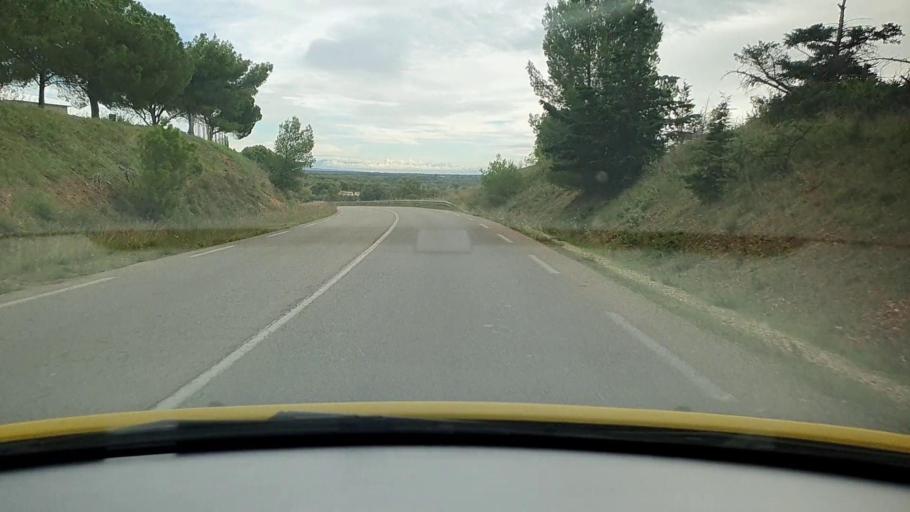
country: FR
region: Languedoc-Roussillon
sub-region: Departement du Gard
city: Saint-Gilles
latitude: 43.6817
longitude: 4.4370
